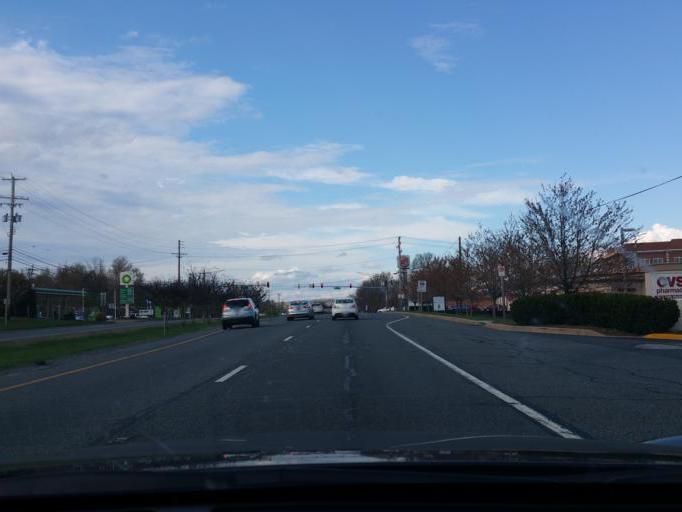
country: US
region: Maryland
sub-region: Harford County
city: Havre de Grace
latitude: 39.5450
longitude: -76.1074
